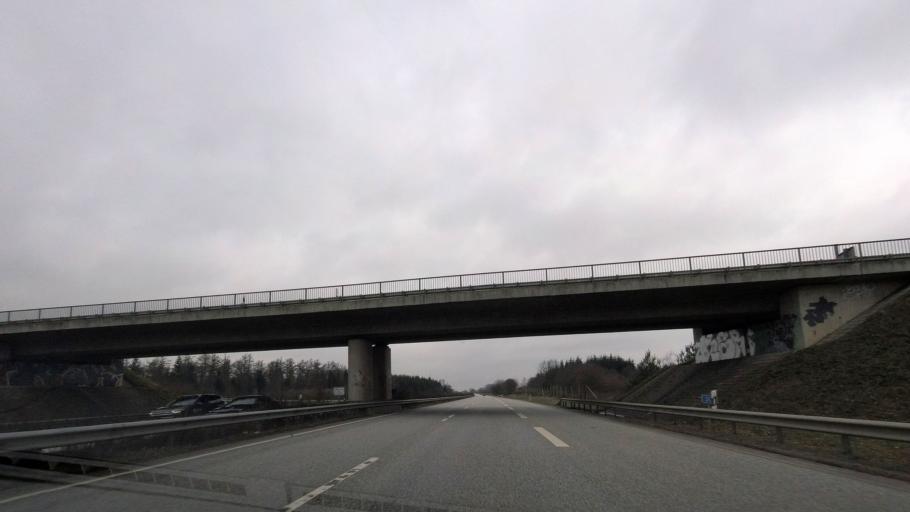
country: DE
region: Schleswig-Holstein
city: Trappenkamp
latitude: 54.0409
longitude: 10.2387
